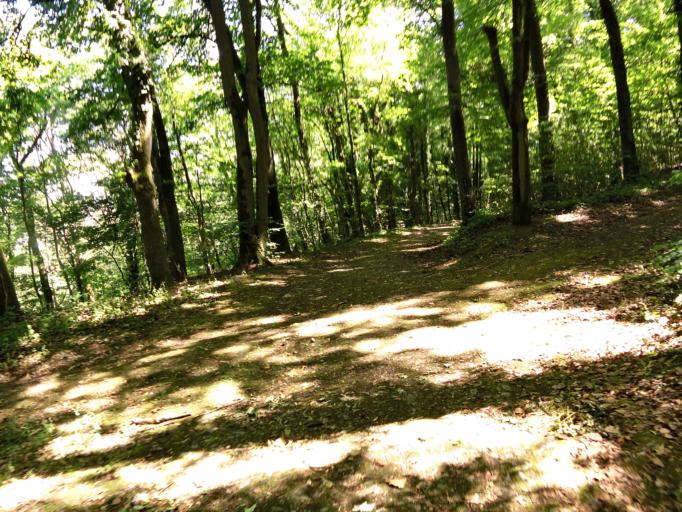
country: DE
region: Bavaria
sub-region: Regierungsbezirk Unterfranken
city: Hochberg
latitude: 49.7833
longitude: 9.9092
